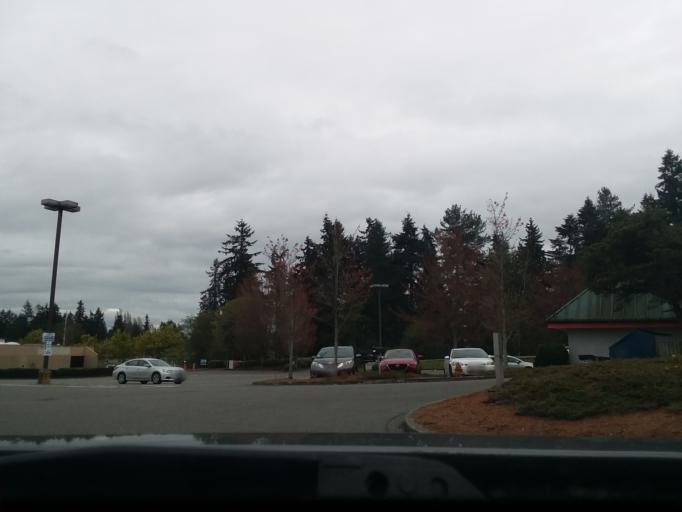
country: US
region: Washington
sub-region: King County
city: Shoreline
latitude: 47.7412
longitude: -122.3499
